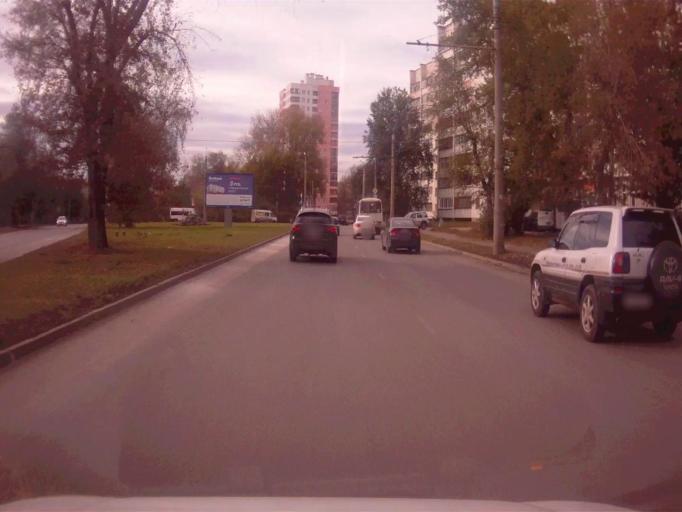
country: RU
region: Chelyabinsk
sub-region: Gorod Chelyabinsk
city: Chelyabinsk
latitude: 55.1166
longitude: 61.4397
